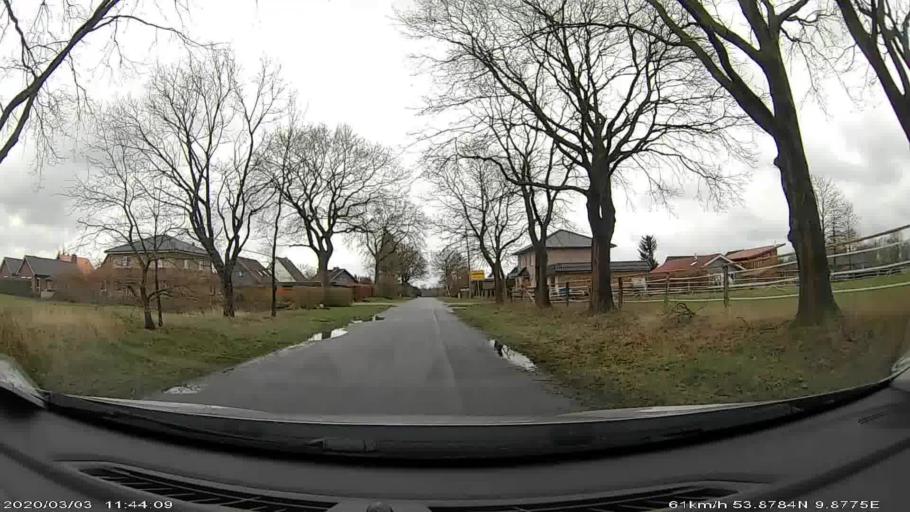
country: DE
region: Schleswig-Holstein
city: Lentfohrden
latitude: 53.8773
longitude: 9.8794
